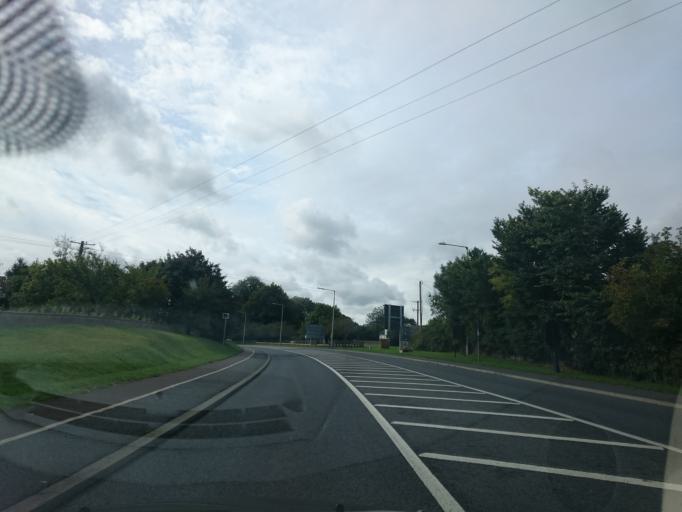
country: IE
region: Leinster
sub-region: Kilkenny
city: Kilkenny
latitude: 52.6337
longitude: -7.2521
